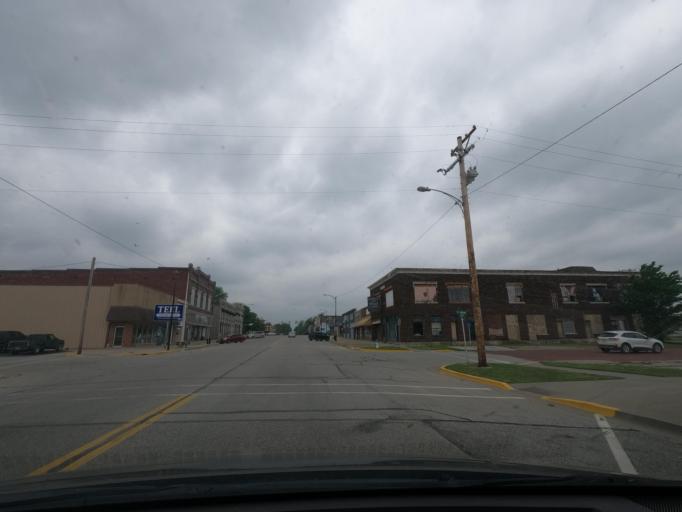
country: US
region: Kansas
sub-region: Cherokee County
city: Columbus
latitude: 37.1709
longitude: -94.8411
